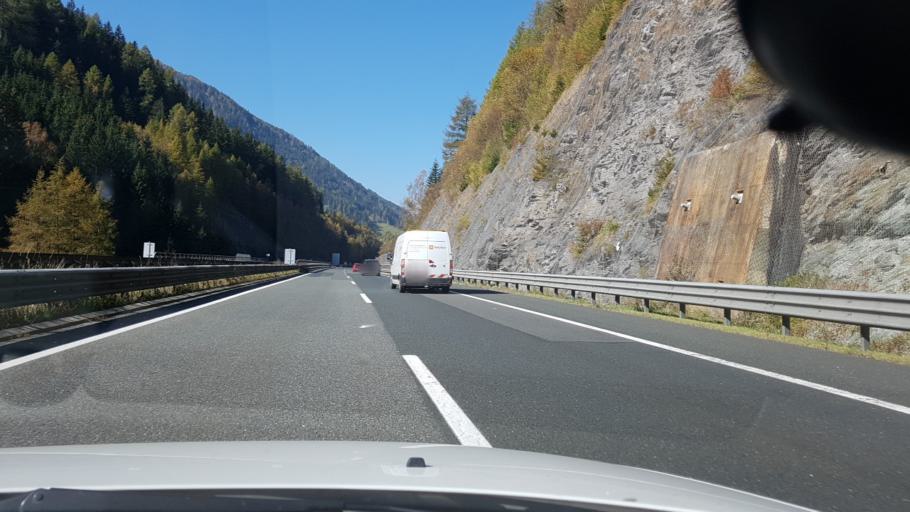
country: AT
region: Salzburg
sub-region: Politischer Bezirk Tamsweg
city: Zederhaus
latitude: 47.1379
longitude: 13.5370
